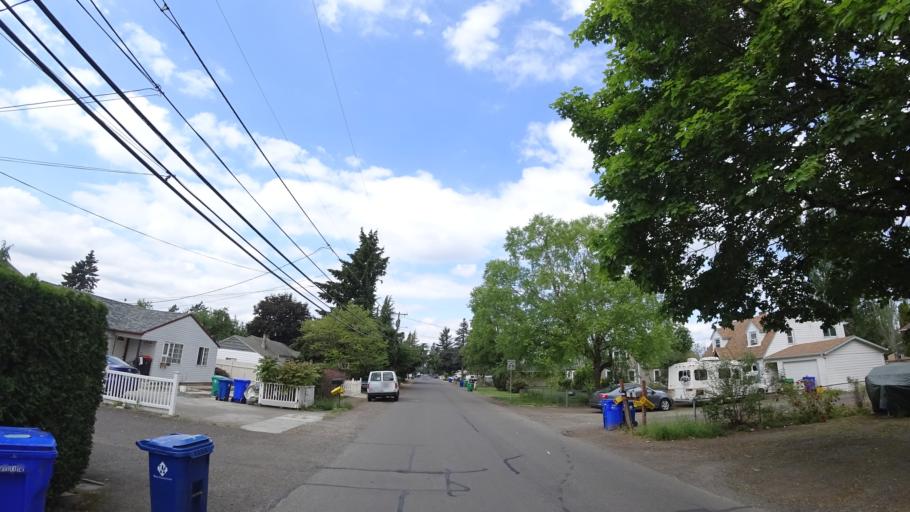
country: US
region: Oregon
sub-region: Multnomah County
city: Gresham
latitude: 45.5054
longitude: -122.4821
